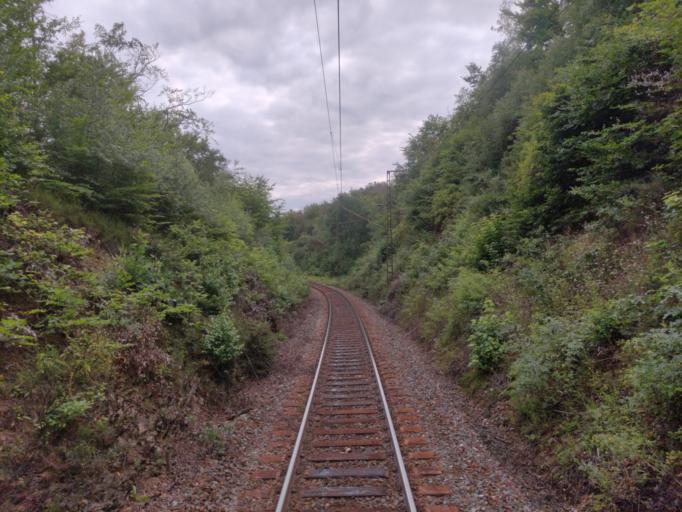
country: DE
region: Saxony-Anhalt
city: Huttenrode
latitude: 51.7895
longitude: 10.9246
